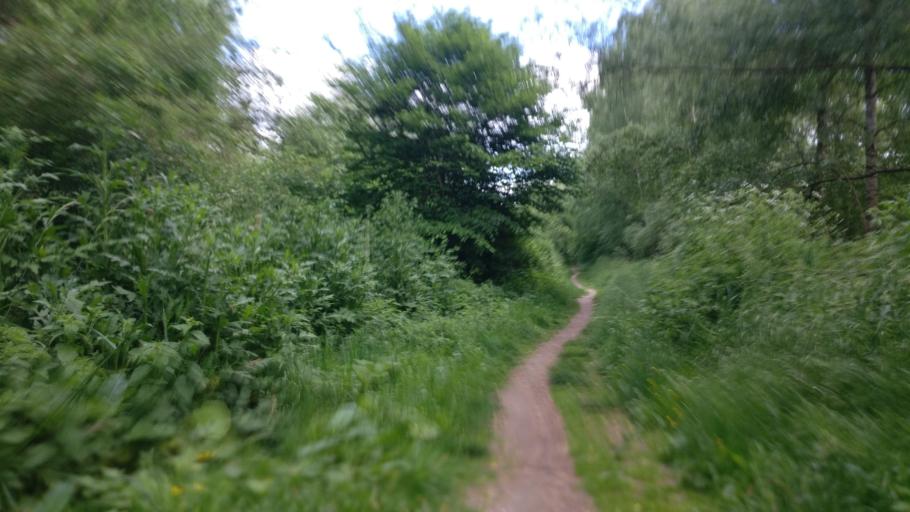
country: DE
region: North Rhine-Westphalia
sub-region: Regierungsbezirk Detmold
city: Lage
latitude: 52.0018
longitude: 8.7759
